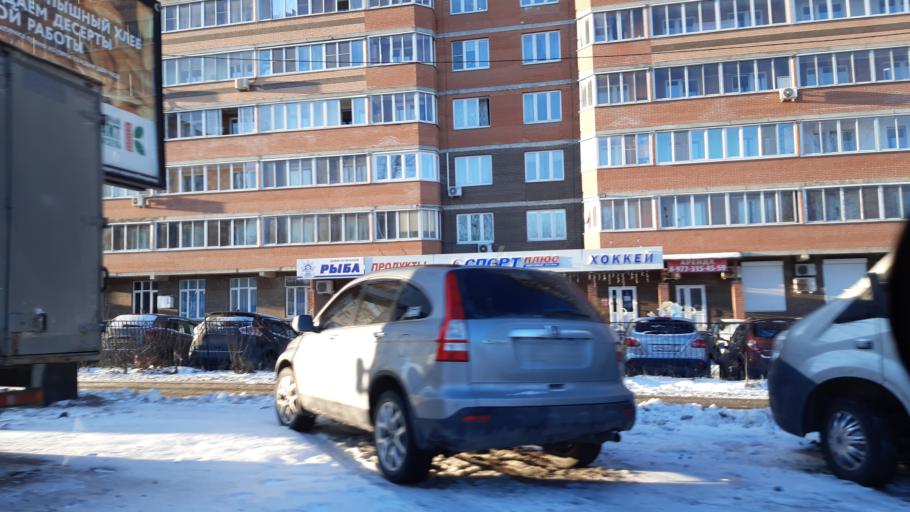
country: RU
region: Moskovskaya
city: Skoropuskovskiy
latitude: 56.3333
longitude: 38.1569
